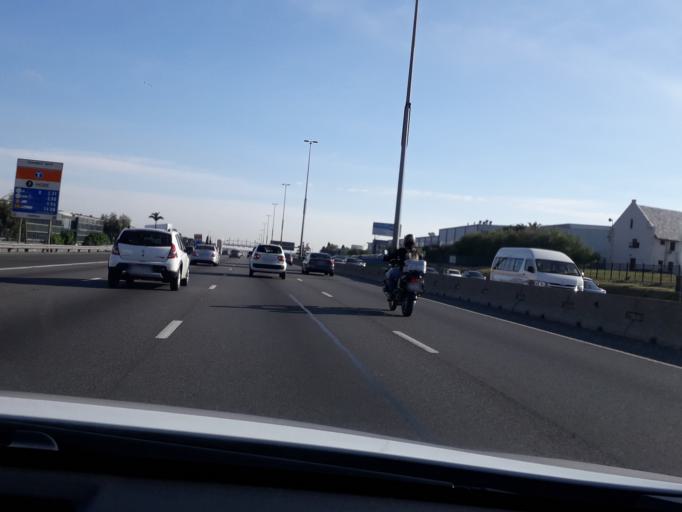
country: ZA
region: Gauteng
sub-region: City of Johannesburg Metropolitan Municipality
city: Midrand
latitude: -25.9741
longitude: 28.1281
